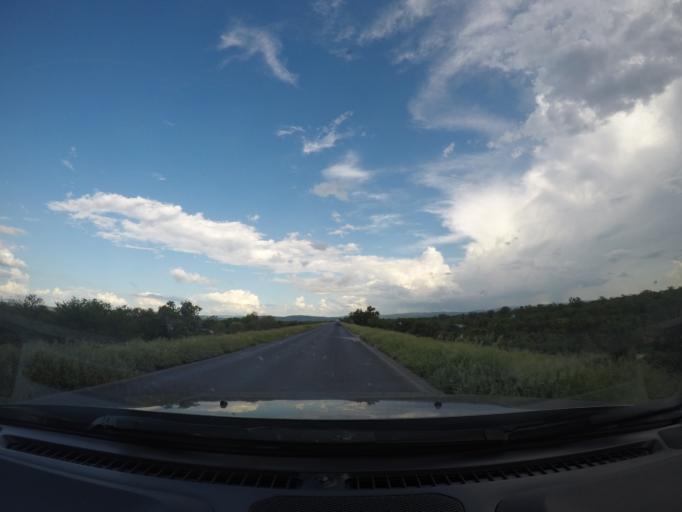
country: BR
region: Bahia
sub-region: Ibotirama
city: Ibotirama
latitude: -12.1676
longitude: -43.2727
